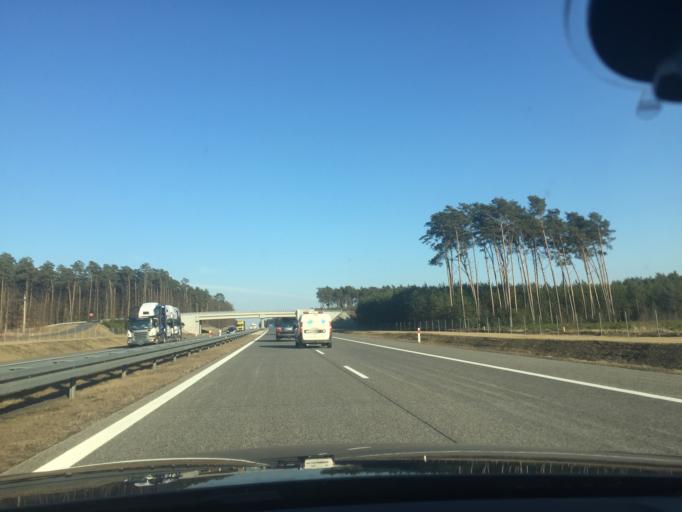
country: PL
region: Greater Poland Voivodeship
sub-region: Powiat nowotomyski
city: Nowy Tomysl
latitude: 52.3523
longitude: 16.0627
